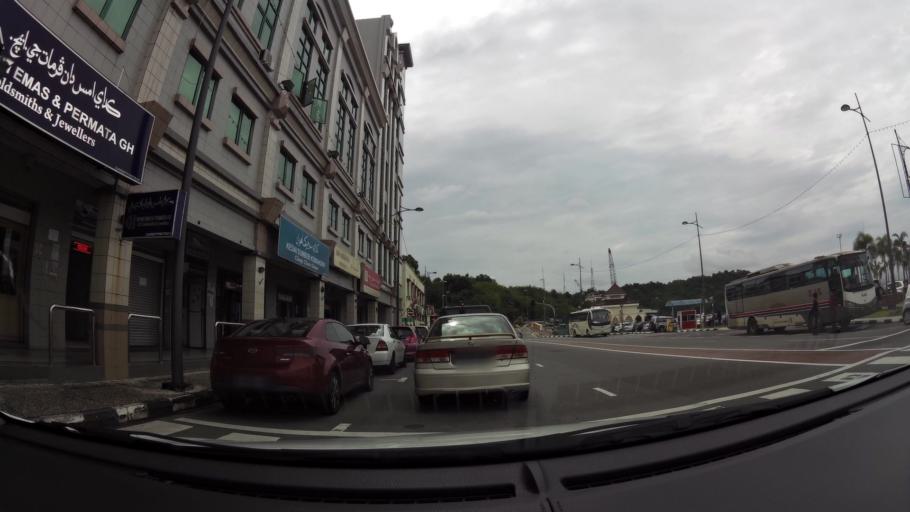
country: BN
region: Brunei and Muara
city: Bandar Seri Begawan
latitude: 4.8872
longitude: 114.9437
